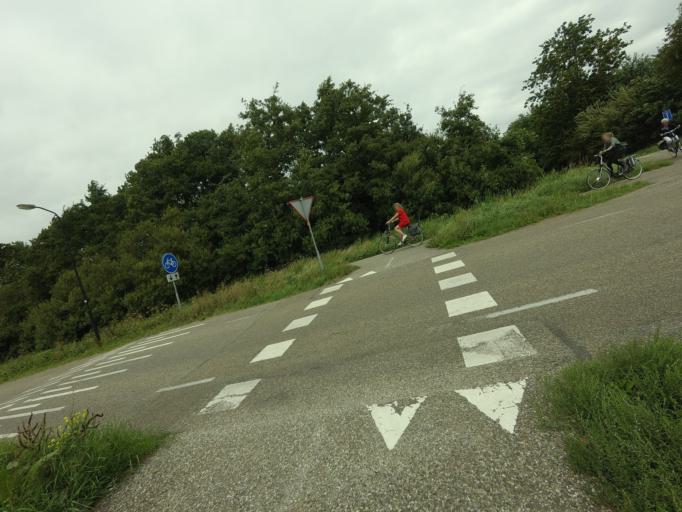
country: NL
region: Utrecht
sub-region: Gemeente De Ronde Venen
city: Mijdrecht
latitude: 52.1868
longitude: 4.9291
